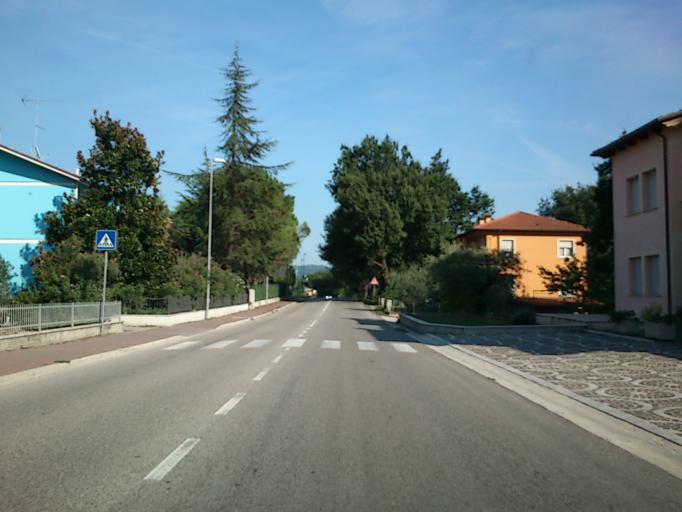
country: IT
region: The Marches
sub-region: Provincia di Pesaro e Urbino
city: Canavaccio
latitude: 43.6930
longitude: 12.7033
